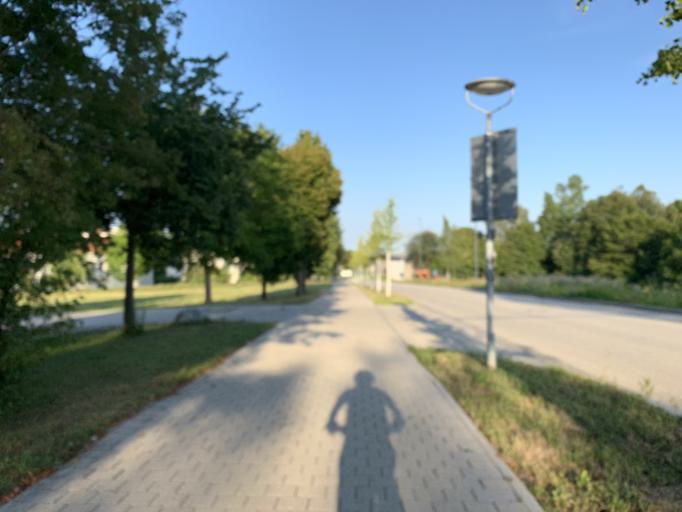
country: DE
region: Bavaria
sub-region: Upper Bavaria
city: Freising
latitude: 48.4041
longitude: 11.7242
